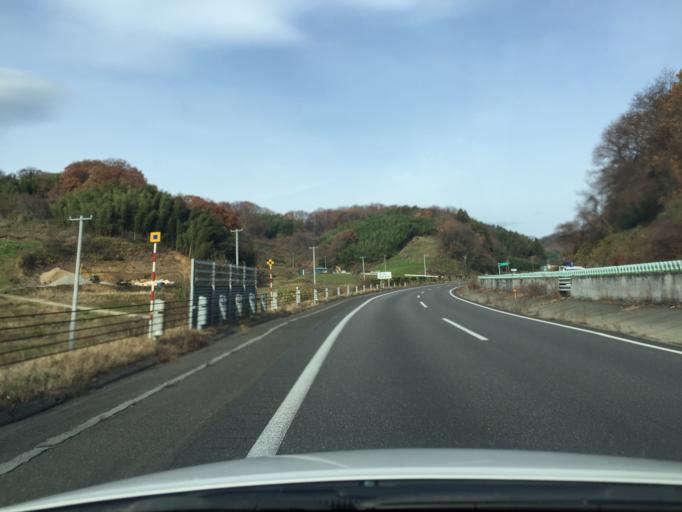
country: JP
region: Fukushima
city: Nihommatsu
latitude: 37.5955
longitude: 140.4184
